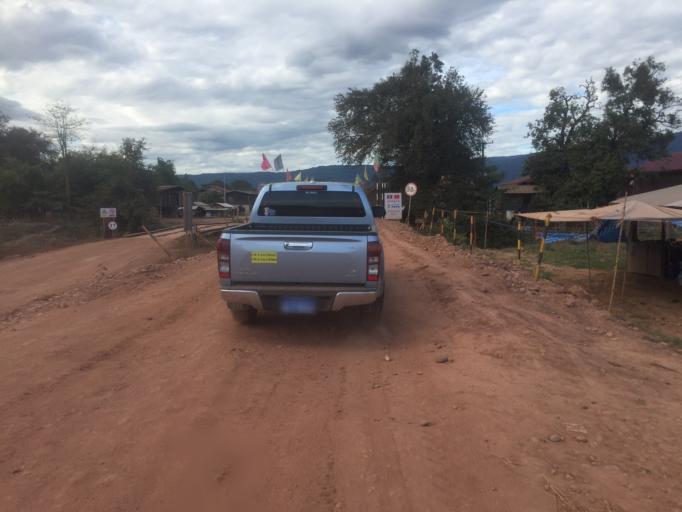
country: LA
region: Attapu
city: Attapu
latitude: 14.6953
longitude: 106.5327
